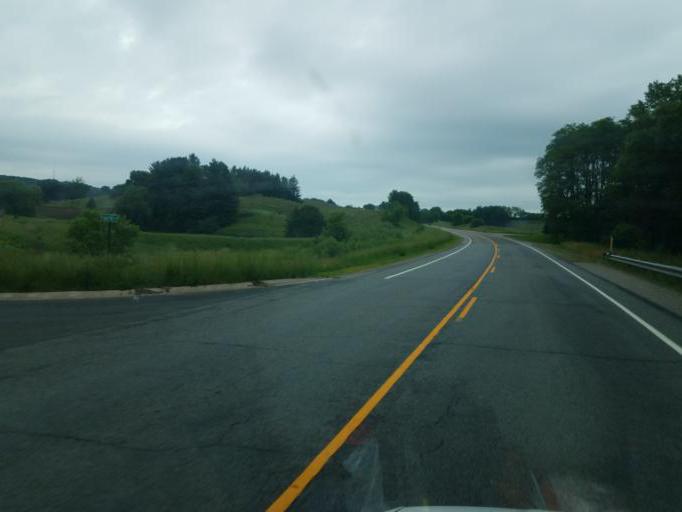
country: US
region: Wisconsin
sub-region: Juneau County
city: Elroy
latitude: 43.7750
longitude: -90.2069
